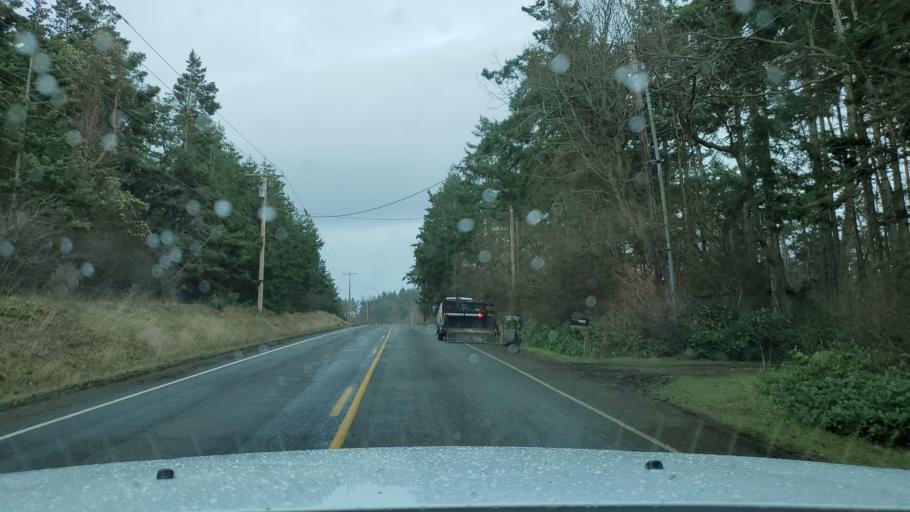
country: US
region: Washington
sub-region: Island County
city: Ault Field
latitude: 48.3078
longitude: -122.7091
